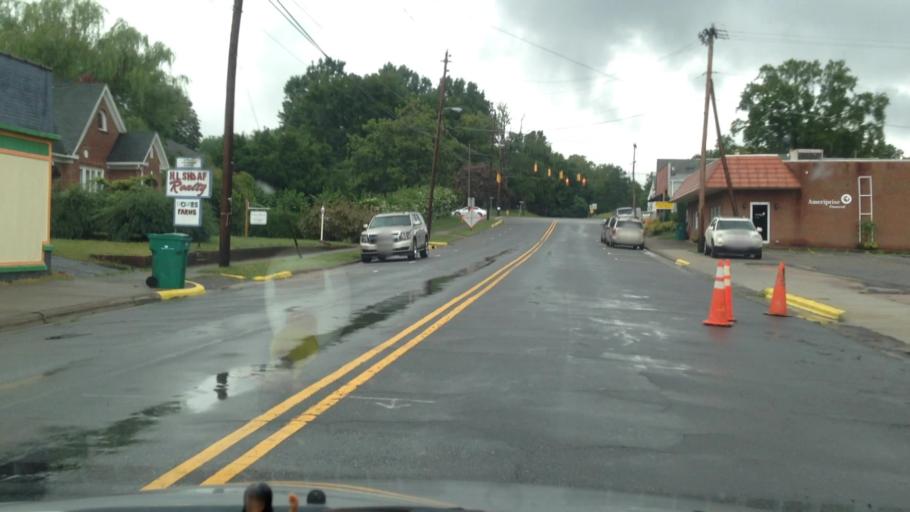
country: US
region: North Carolina
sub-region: Rockingham County
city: Madison
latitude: 36.3876
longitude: -79.9617
